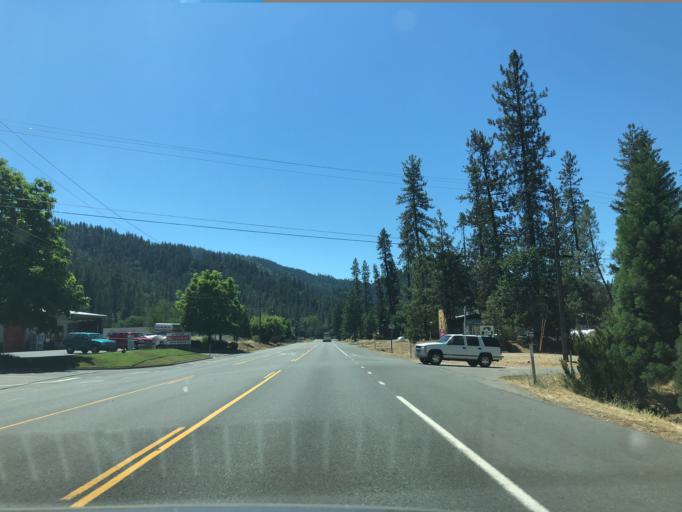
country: US
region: California
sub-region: Trinity County
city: Weaverville
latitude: 40.7182
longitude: -122.9272
